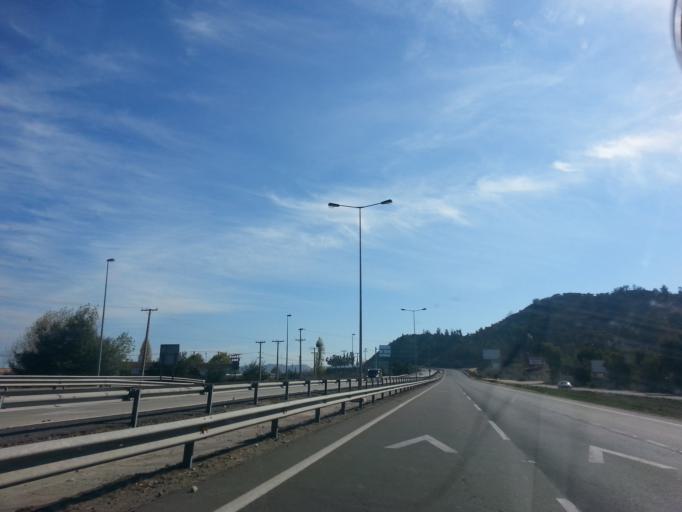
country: CL
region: Valparaiso
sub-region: Provincia de Marga Marga
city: Quilpue
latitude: -33.3276
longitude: -71.3906
